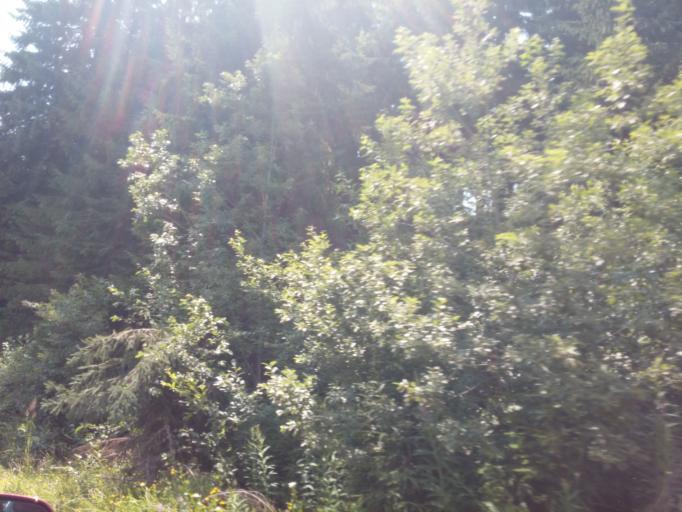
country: RO
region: Valcea
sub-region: Comuna Voineasa
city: Voineasa
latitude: 45.4286
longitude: 23.8112
